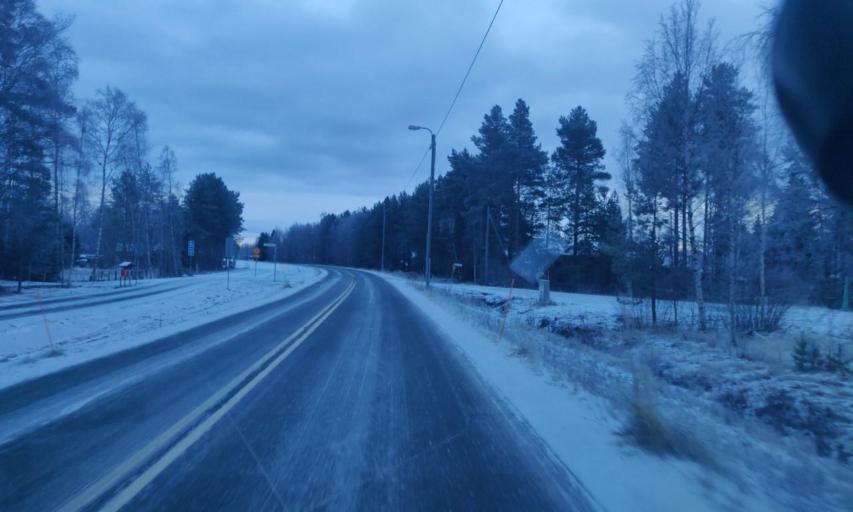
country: FI
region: Northern Ostrobothnia
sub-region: Oulu
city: Oulunsalo
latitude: 64.9884
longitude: 25.2584
